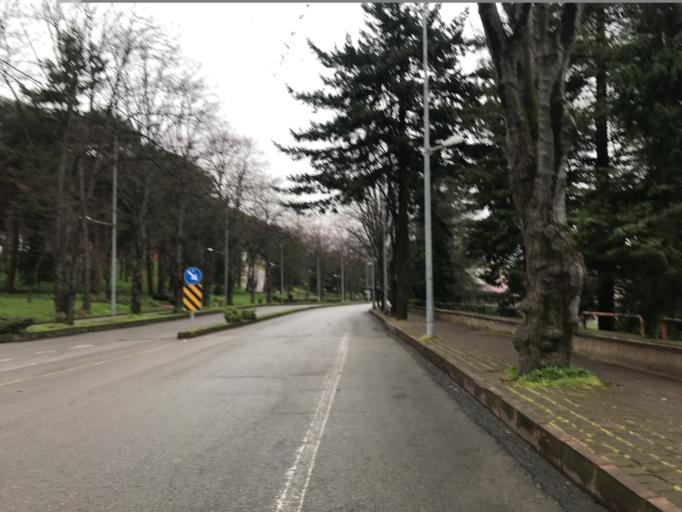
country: TR
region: Trabzon
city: Trabzon
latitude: 40.9977
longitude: 39.7681
